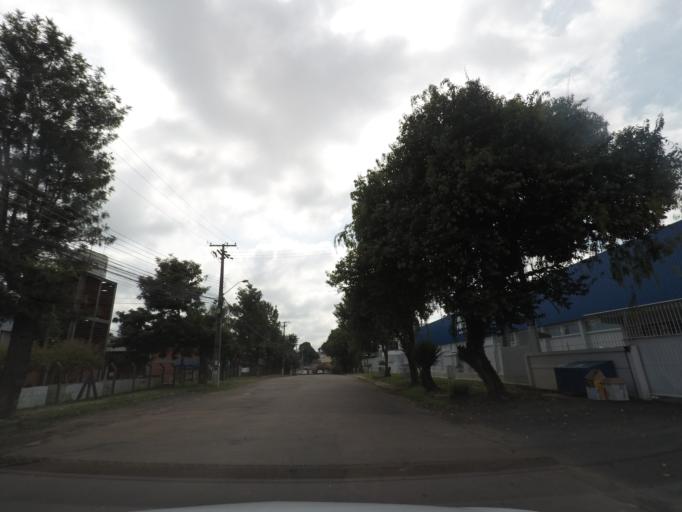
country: BR
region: Parana
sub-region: Curitiba
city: Curitiba
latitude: -25.4933
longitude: -49.3288
